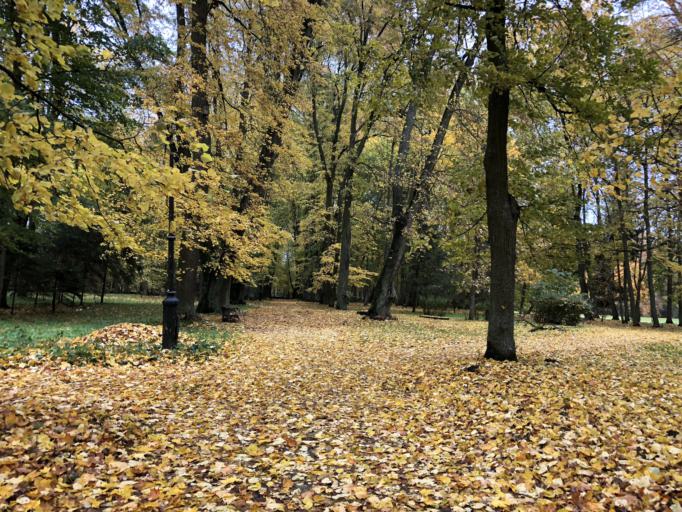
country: BY
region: Minsk
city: Nyasvizh
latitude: 53.2268
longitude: 26.6937
